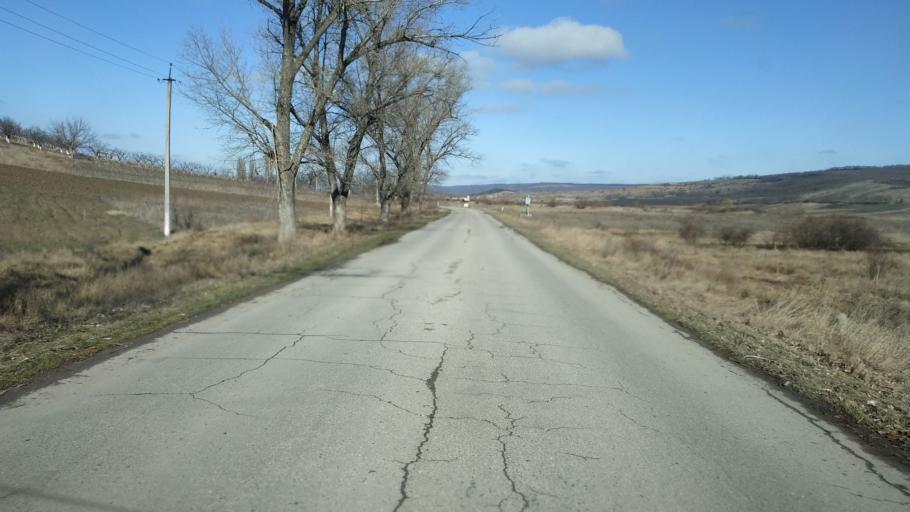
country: MD
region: Hincesti
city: Hincesti
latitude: 46.9425
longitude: 28.6249
